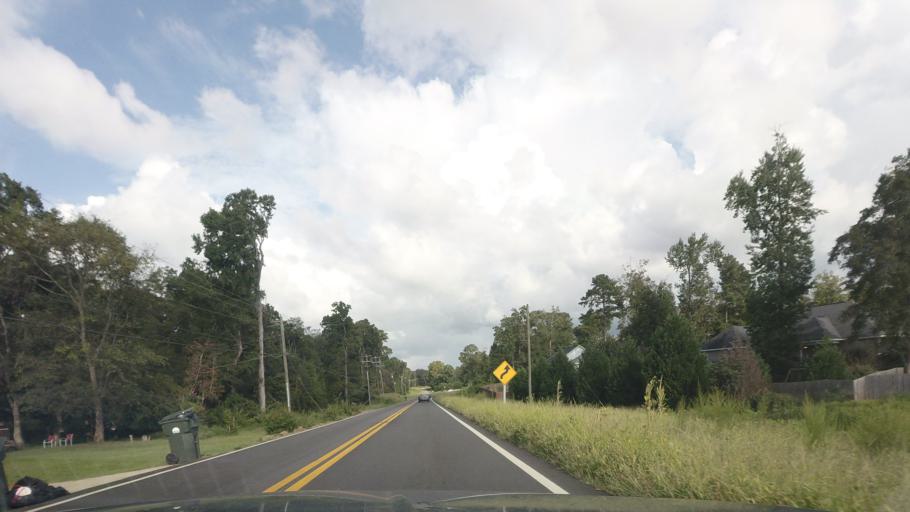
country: US
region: Georgia
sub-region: Houston County
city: Centerville
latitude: 32.6350
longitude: -83.7152
